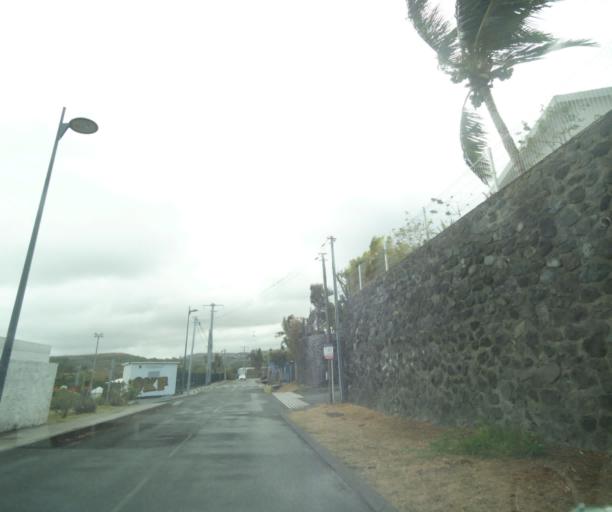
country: RE
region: Reunion
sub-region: Reunion
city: Saint-Paul
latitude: -21.0458
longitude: 55.2258
